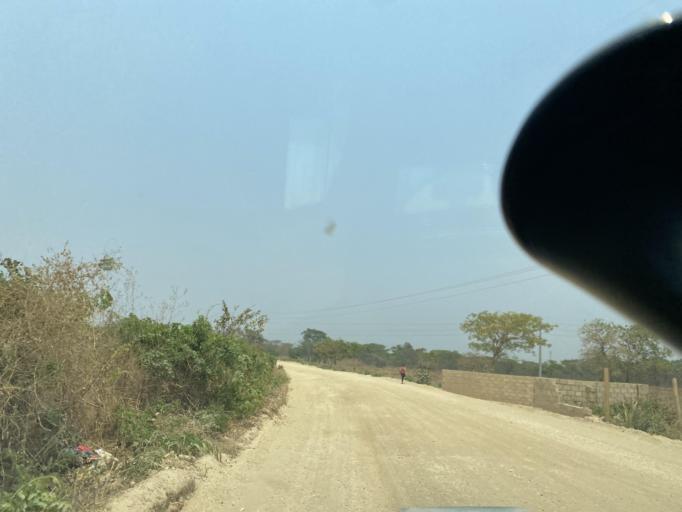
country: ZM
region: Lusaka
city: Lusaka
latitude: -15.5308
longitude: 28.3419
